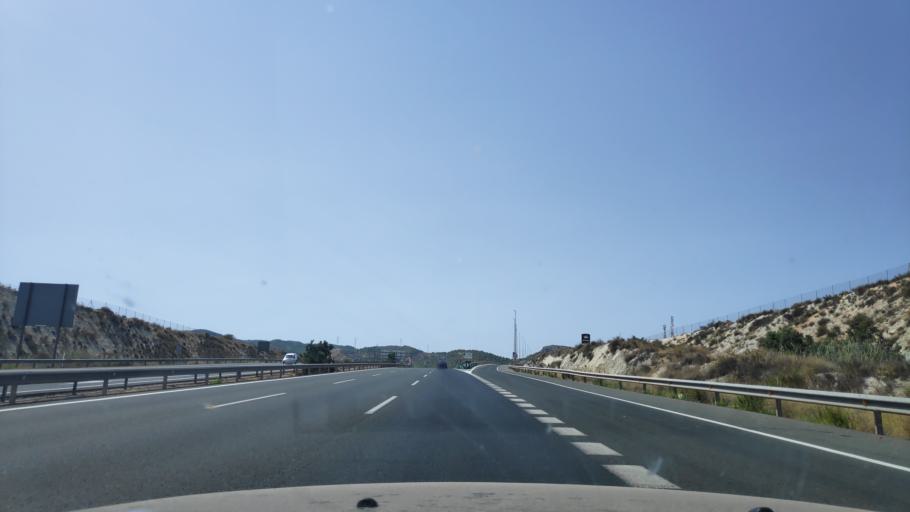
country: ES
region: Murcia
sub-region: Murcia
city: Murcia
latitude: 37.8814
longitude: -1.1332
